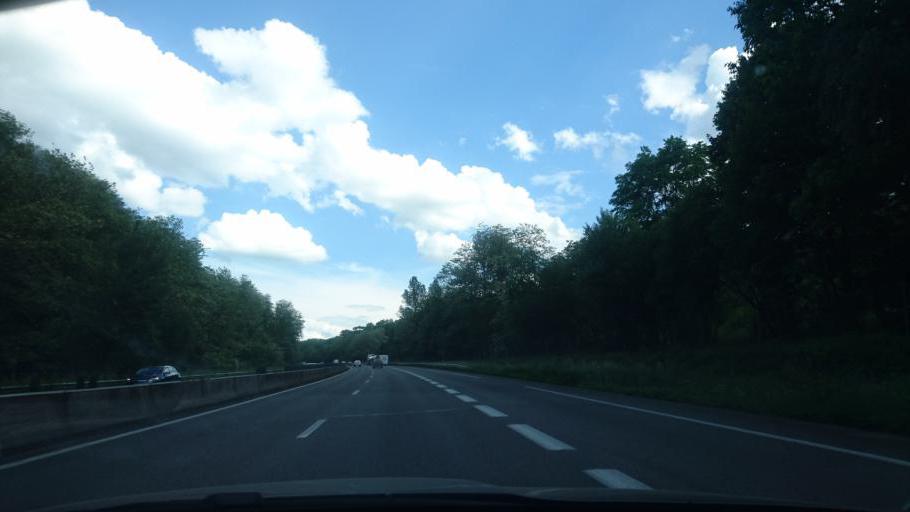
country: FR
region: Midi-Pyrenees
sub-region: Departement des Hautes-Pyrenees
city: Capvern
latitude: 43.1513
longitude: 0.2943
